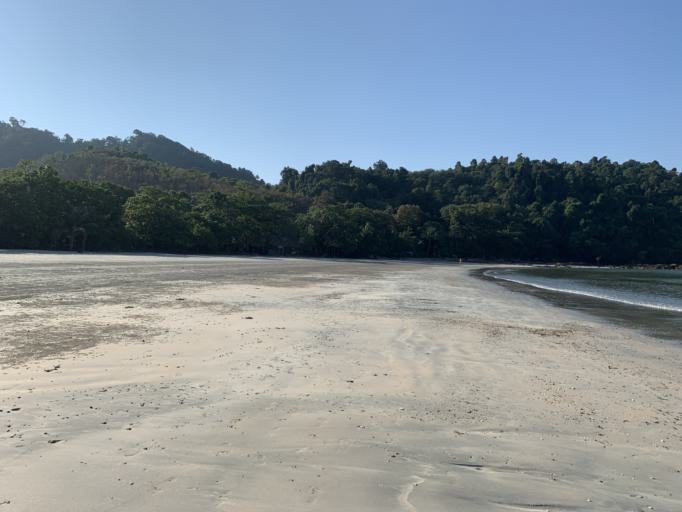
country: TH
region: Ranong
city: Kapoe
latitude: 9.7125
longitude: 98.3969
